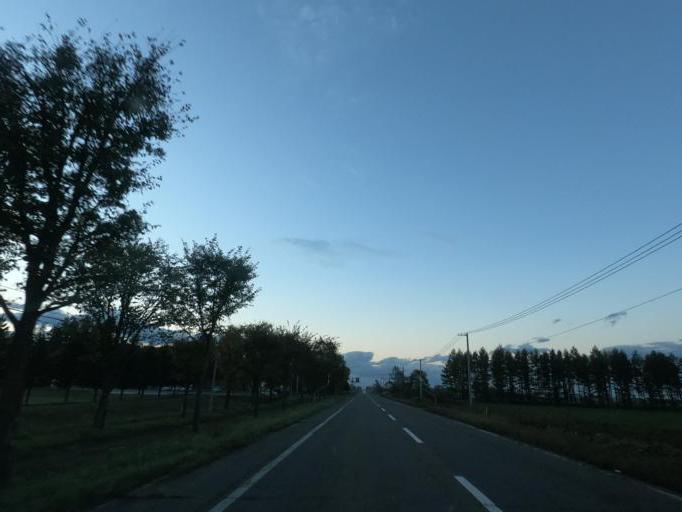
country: JP
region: Hokkaido
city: Obihiro
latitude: 42.6442
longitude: 143.1997
